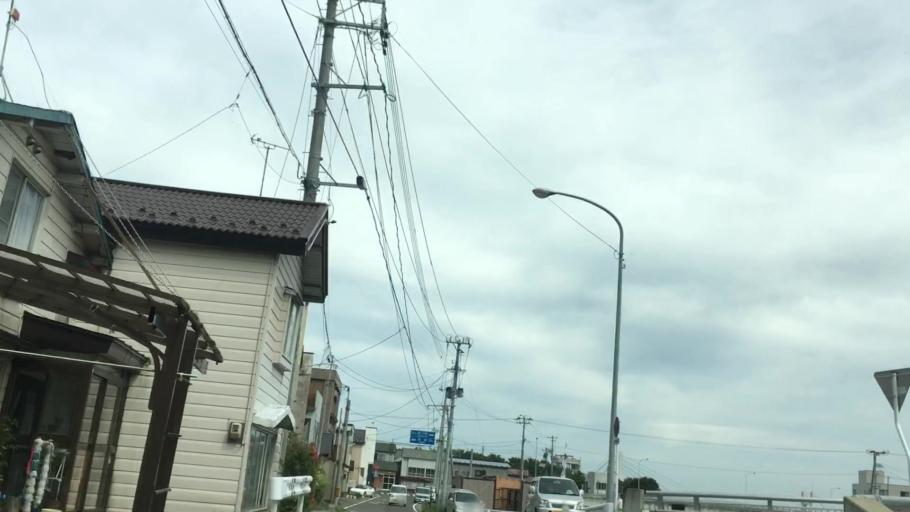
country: JP
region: Aomori
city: Shimokizukuri
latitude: 40.7768
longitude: 140.2171
